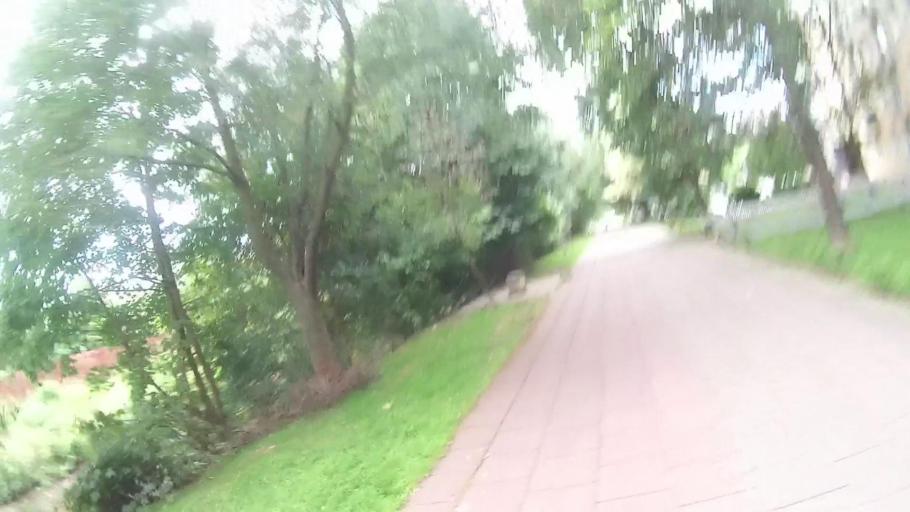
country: PL
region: Masovian Voivodeship
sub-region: Warszawa
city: Praga Poludnie
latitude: 52.2378
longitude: 21.0658
